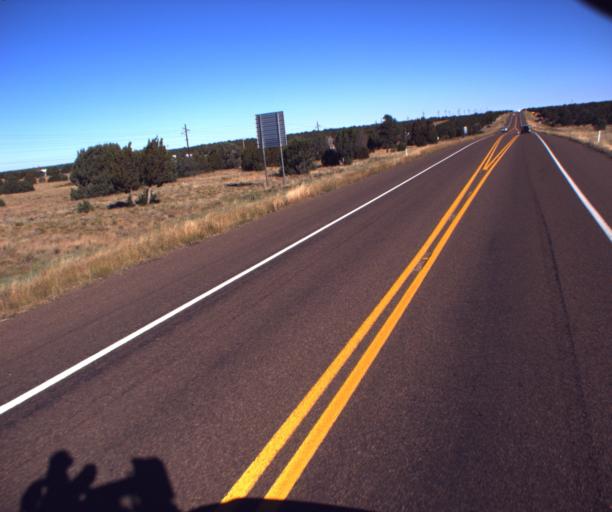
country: US
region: Arizona
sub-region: Navajo County
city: Show Low
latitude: 34.2680
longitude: -110.0223
